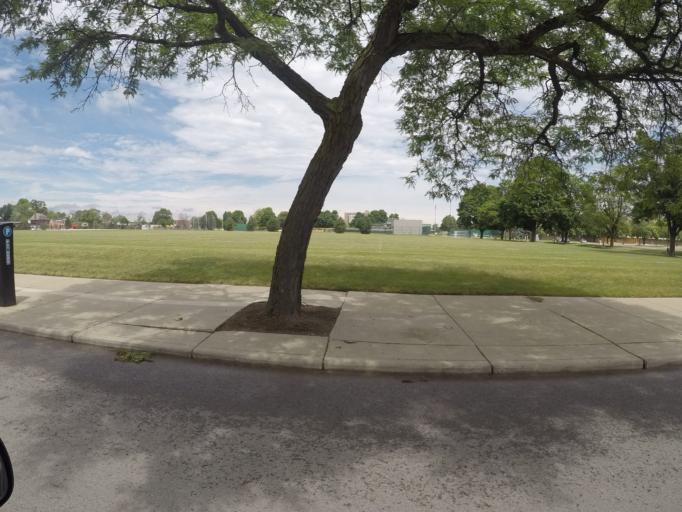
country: US
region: Michigan
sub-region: Wayne County
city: Detroit
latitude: 42.3530
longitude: -83.0769
